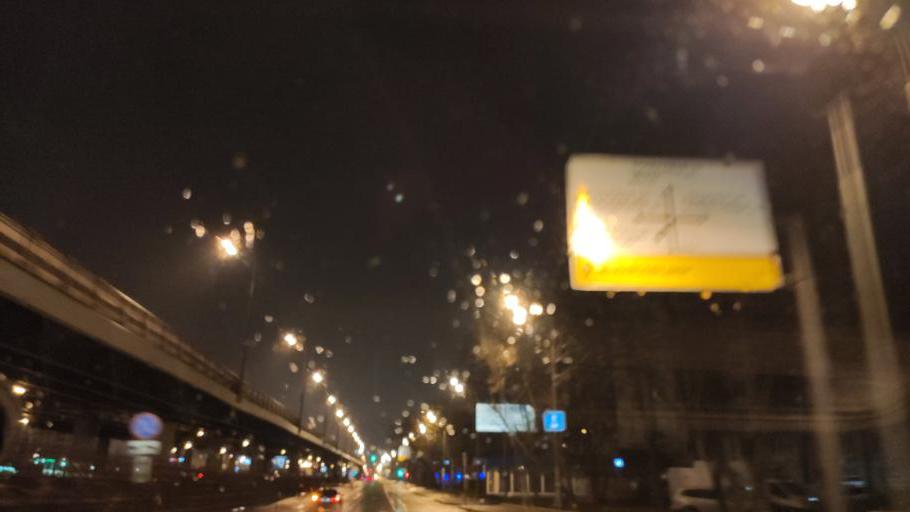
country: RU
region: Moskovskaya
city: Bol'shaya Setun'
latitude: 55.7183
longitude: 37.4128
